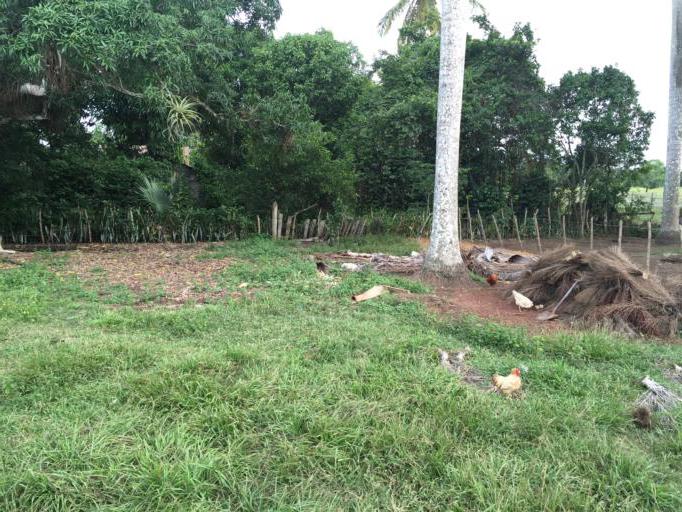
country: CU
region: Camaguey
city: Florida
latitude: 21.4840
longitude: -78.1847
